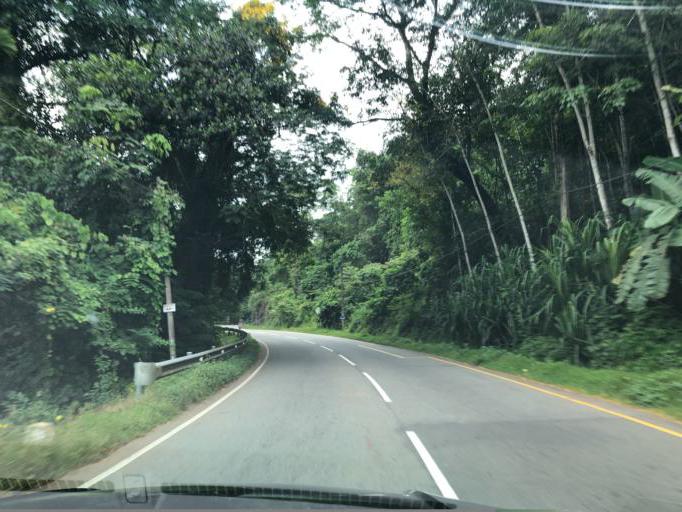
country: LK
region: Western
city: Horana South
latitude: 6.6819
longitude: 80.1319
